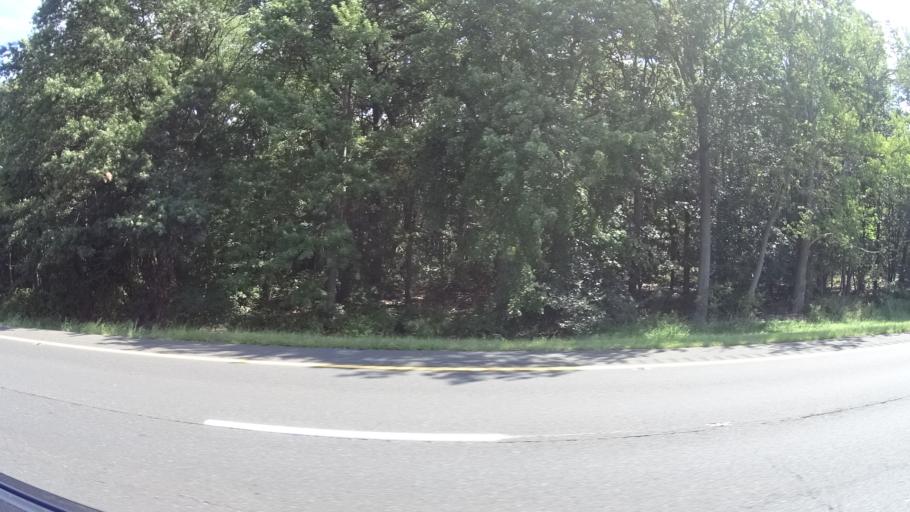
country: US
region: New Jersey
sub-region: Monmouth County
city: Strathmore
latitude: 40.4101
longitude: -74.2005
